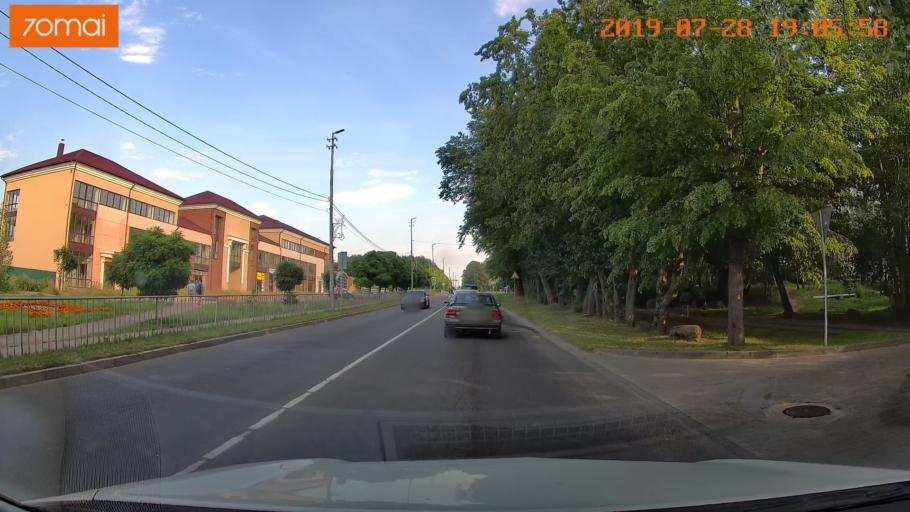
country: RU
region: Kaliningrad
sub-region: Gorod Svetlogorsk
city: Svetlogorsk
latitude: 54.9320
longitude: 20.1641
